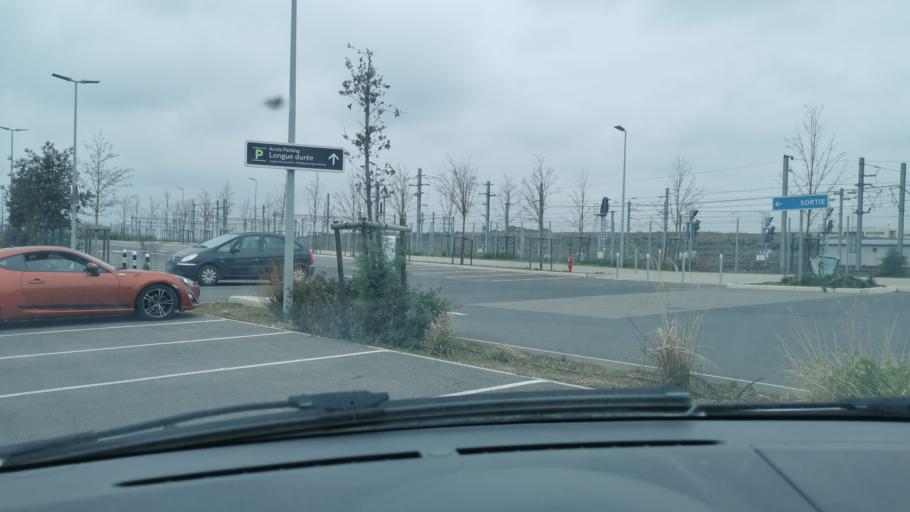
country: FR
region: Languedoc-Roussillon
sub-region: Departement de l'Herault
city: Lattes
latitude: 43.5941
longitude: 3.9234
